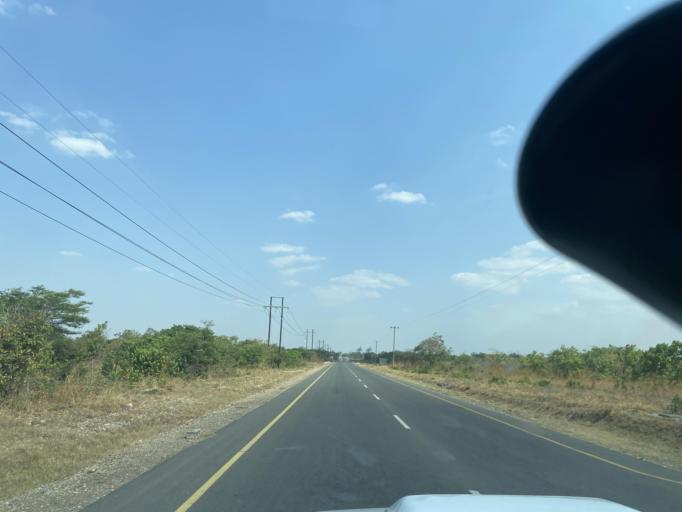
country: ZM
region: Lusaka
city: Lusaka
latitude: -15.3299
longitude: 28.0696
